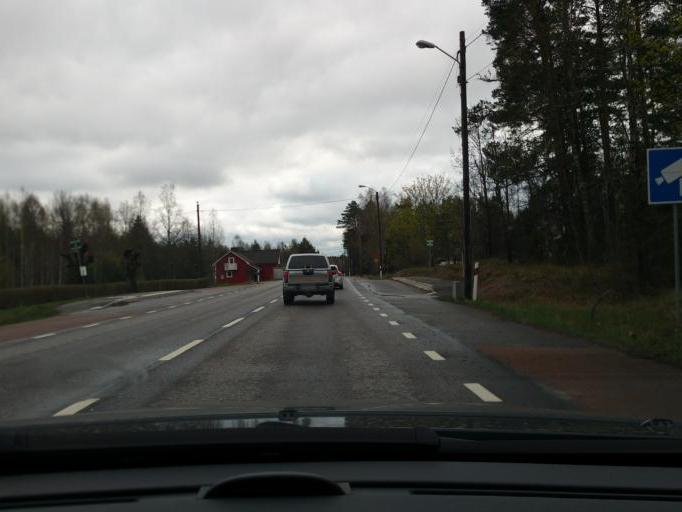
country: SE
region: Kronoberg
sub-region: Vaxjo Kommun
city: Ingelstad
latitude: 56.8238
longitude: 14.8782
